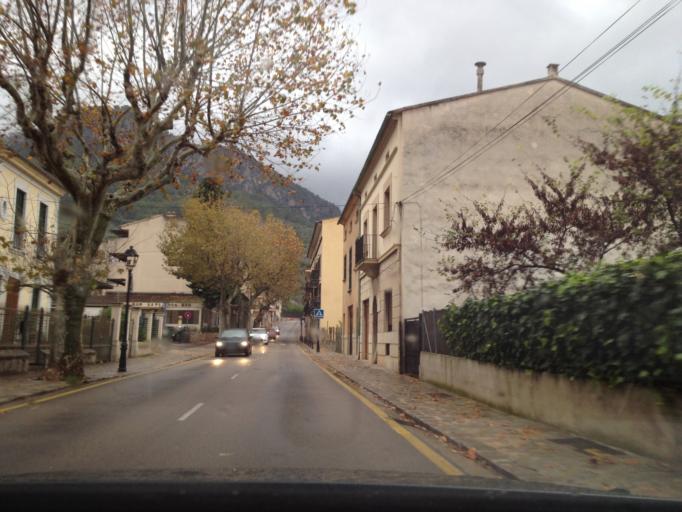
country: ES
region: Balearic Islands
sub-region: Illes Balears
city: Soller
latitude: 39.7678
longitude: 2.7104
